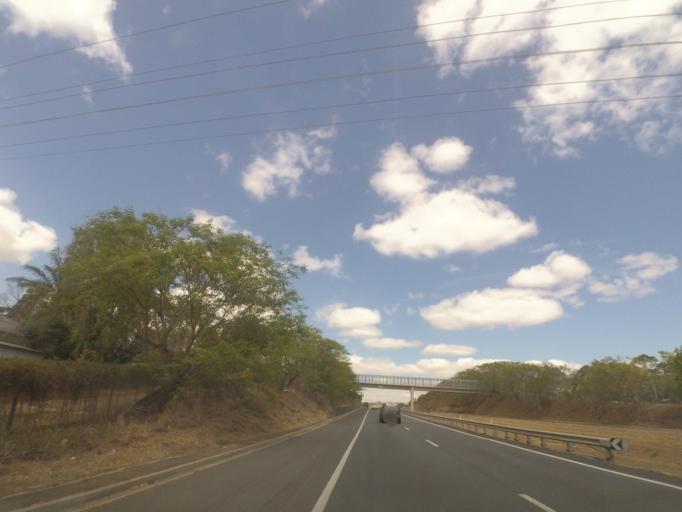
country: AU
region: Queensland
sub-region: Ipswich
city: Thagoona
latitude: -27.5631
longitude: 152.5939
